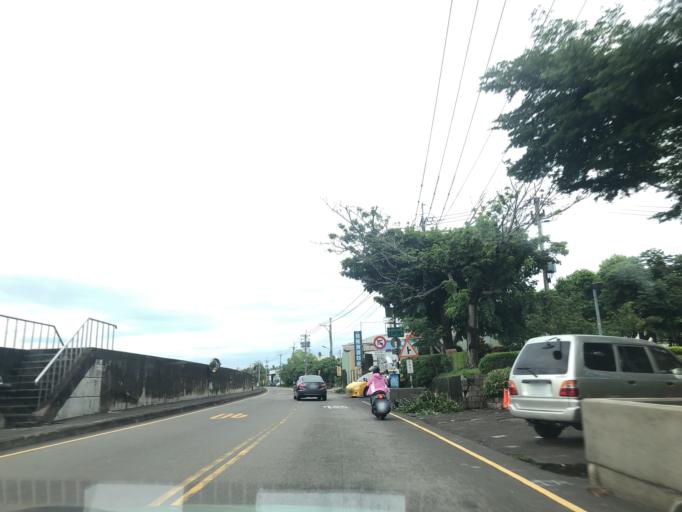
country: TW
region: Taiwan
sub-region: Taichung City
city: Taichung
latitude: 24.1119
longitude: 120.7008
